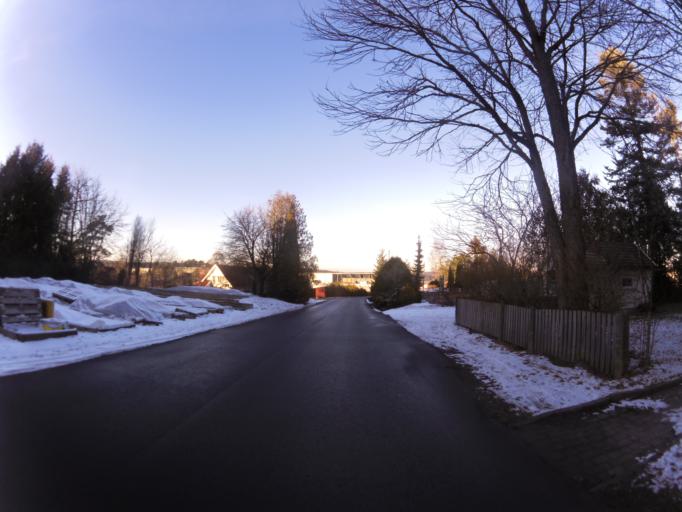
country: NO
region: Ostfold
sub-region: Fredrikstad
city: Lervik
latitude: 59.2627
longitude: 10.8081
